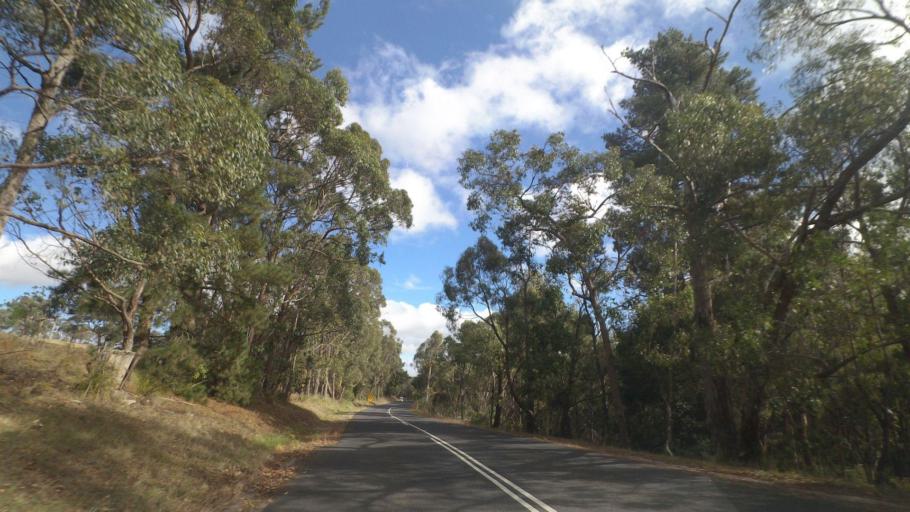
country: AU
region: Victoria
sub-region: Cardinia
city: Garfield
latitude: -38.0536
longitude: 145.6244
